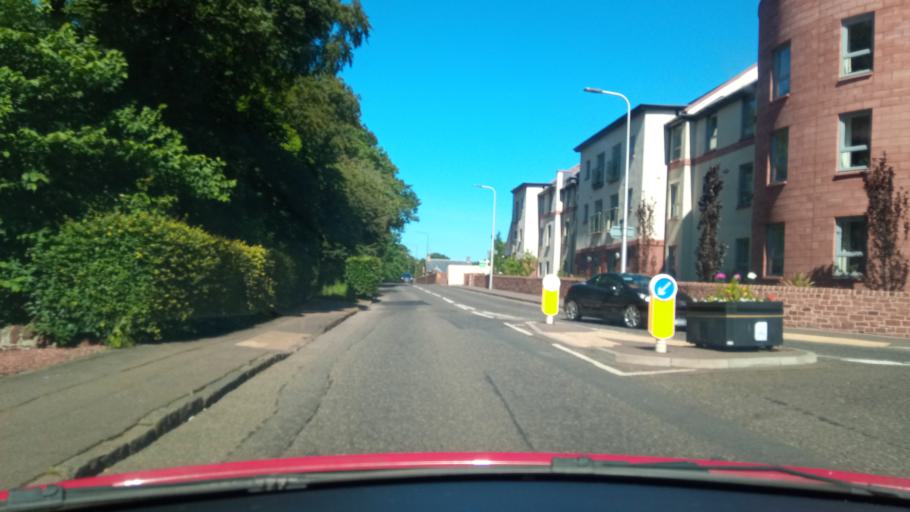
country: GB
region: Scotland
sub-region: East Lothian
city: North Berwick
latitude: 56.0527
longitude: -2.7048
